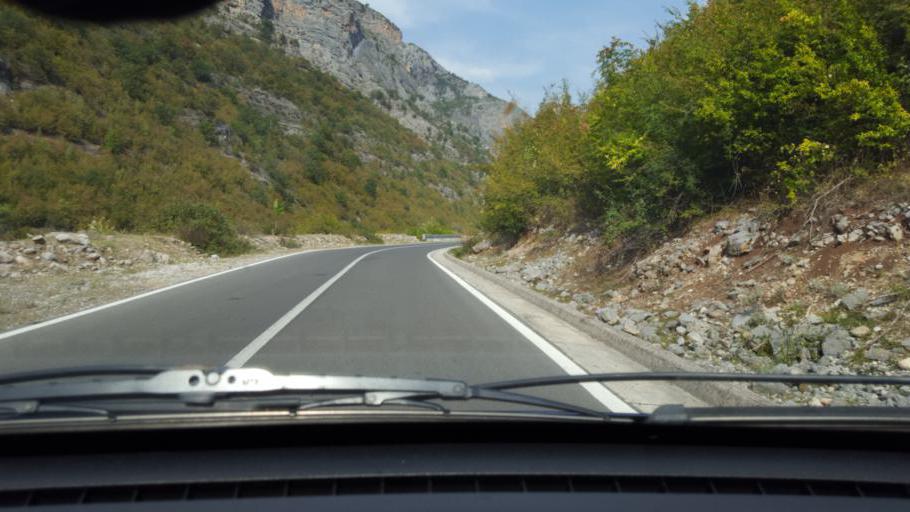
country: AL
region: Shkoder
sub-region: Rrethi i Malesia e Madhe
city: Kastrat
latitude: 42.4439
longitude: 19.5413
